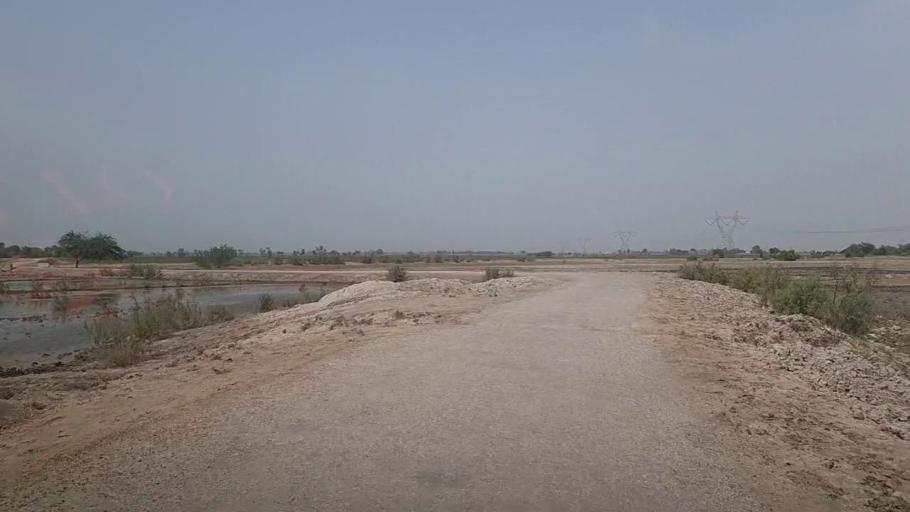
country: PK
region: Sindh
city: Sita Road
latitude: 27.0899
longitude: 67.8560
